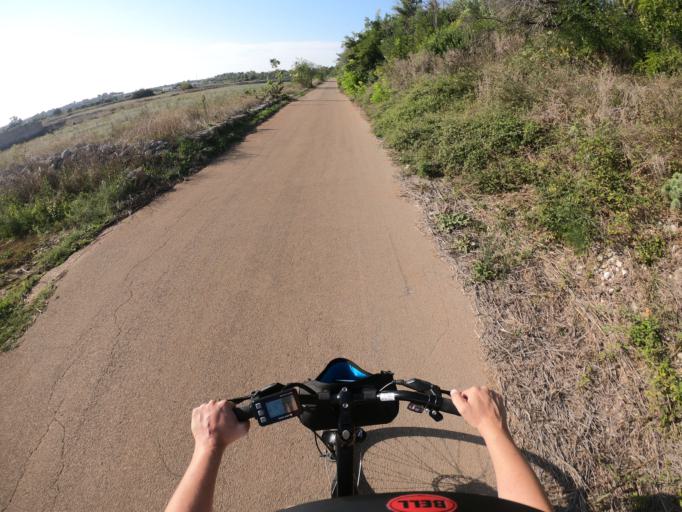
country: IT
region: Apulia
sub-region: Provincia di Lecce
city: Leuca
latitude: 39.8133
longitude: 18.3636
